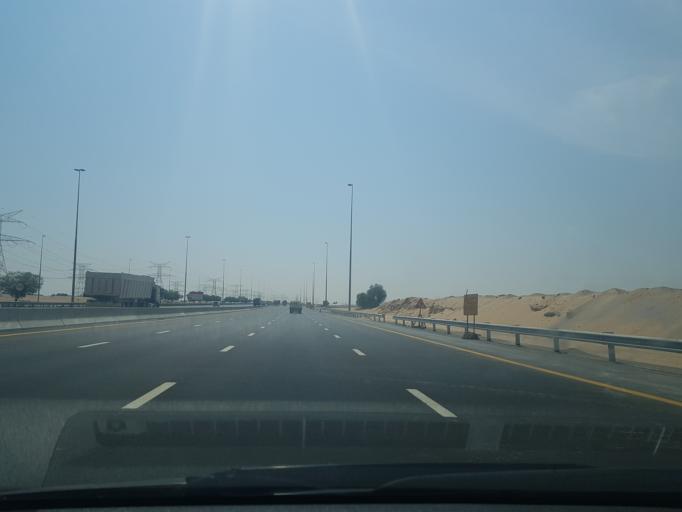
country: AE
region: Ash Shariqah
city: Sharjah
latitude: 25.2312
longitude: 55.5627
